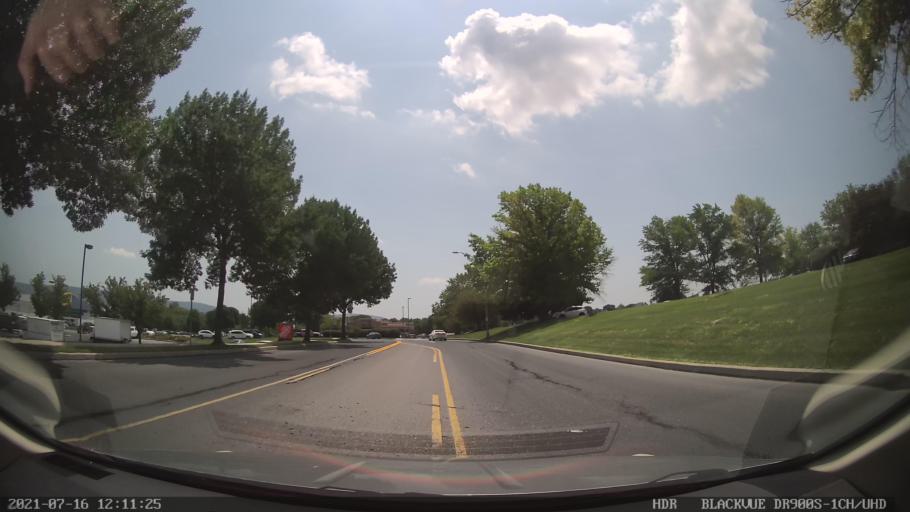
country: US
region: Pennsylvania
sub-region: Berks County
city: Wyomissing Hills
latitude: 40.3479
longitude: -75.9685
